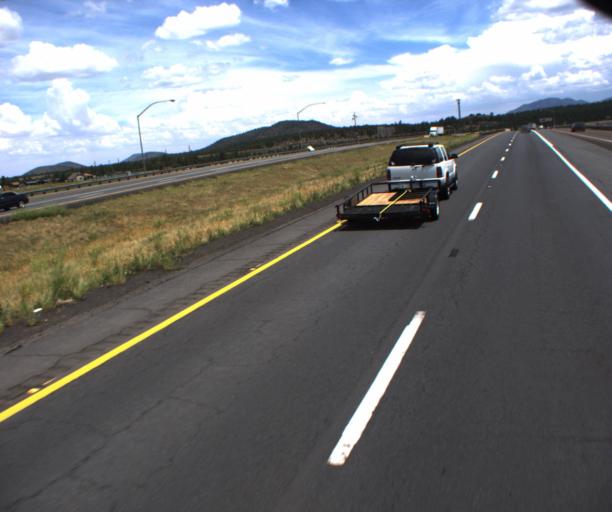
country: US
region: Arizona
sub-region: Coconino County
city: Williams
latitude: 35.2610
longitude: -112.1887
